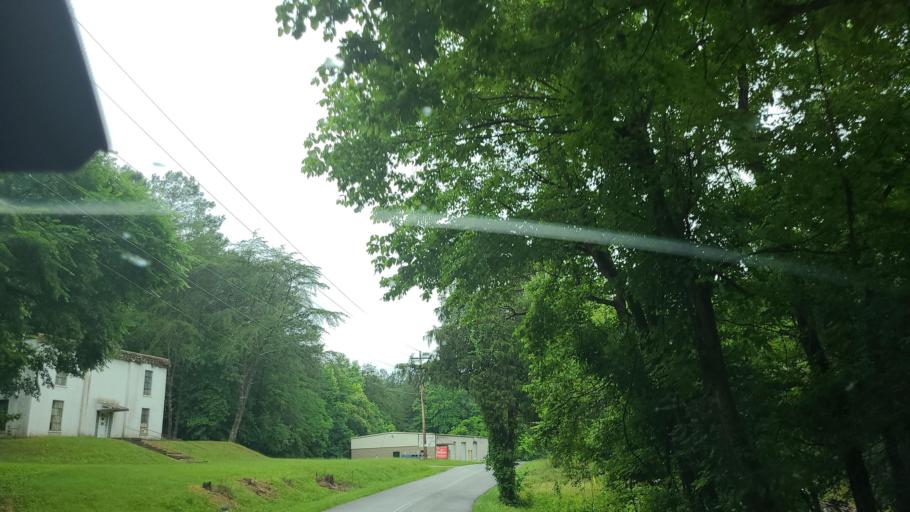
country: US
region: Tennessee
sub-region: Rhea County
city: Dayton
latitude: 35.5051
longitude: -84.9978
